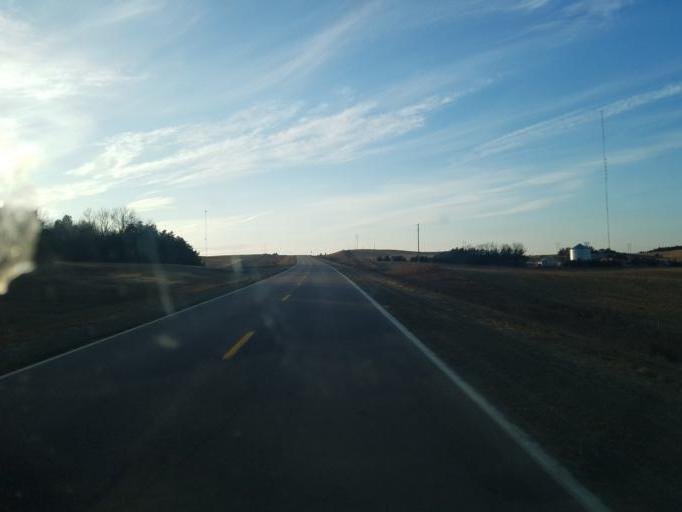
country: US
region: South Dakota
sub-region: Yankton County
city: Yankton
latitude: 42.7285
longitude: -97.3968
